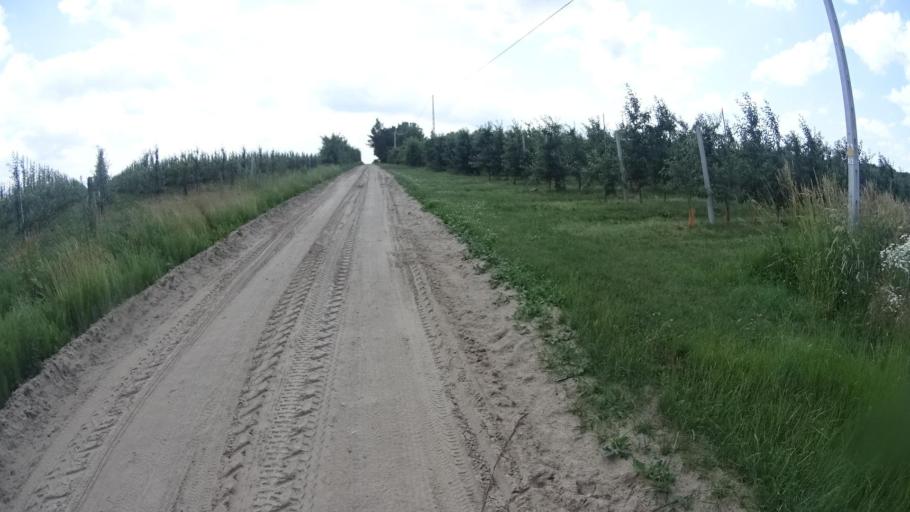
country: PL
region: Masovian Voivodeship
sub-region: Powiat grojecki
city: Goszczyn
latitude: 51.7092
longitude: 20.8300
